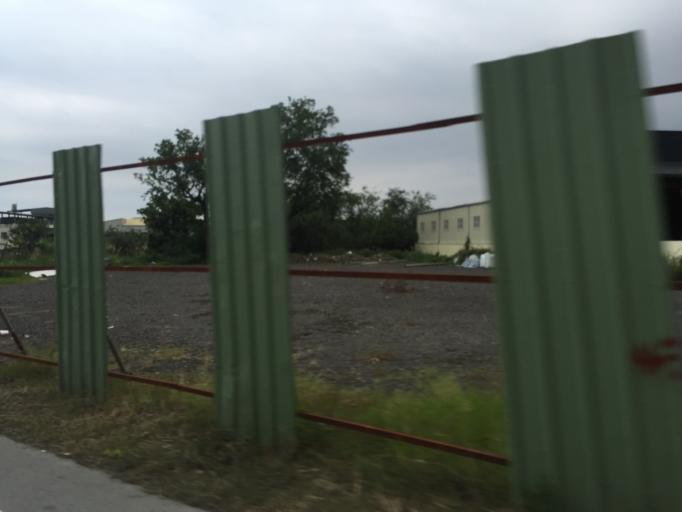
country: TW
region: Taiwan
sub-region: Yilan
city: Yilan
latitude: 24.7801
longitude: 121.7393
